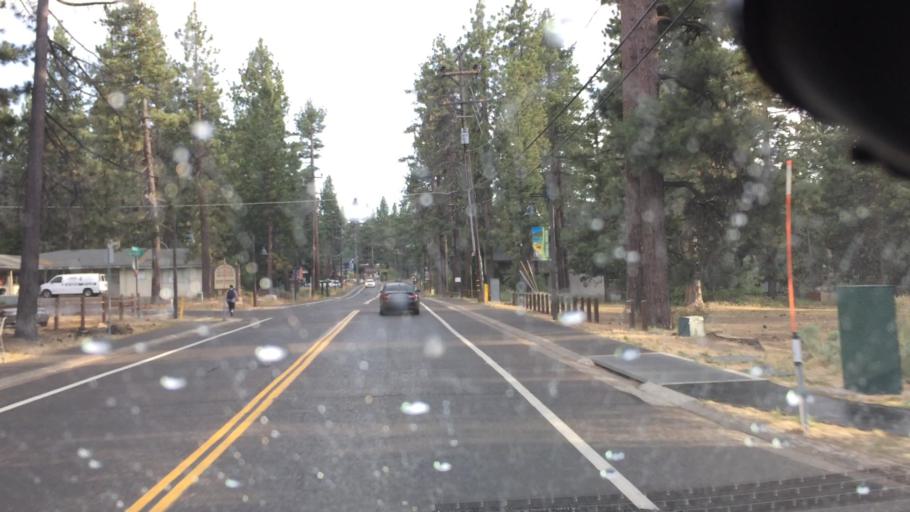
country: US
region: California
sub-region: El Dorado County
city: South Lake Tahoe
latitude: 38.9499
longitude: -119.9481
